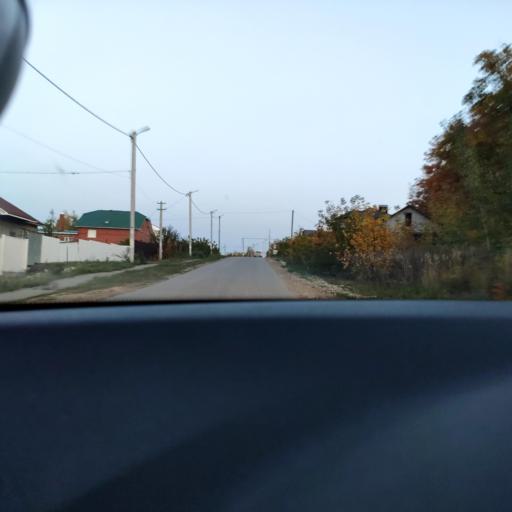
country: RU
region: Samara
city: Novosemeykino
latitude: 53.3827
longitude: 50.3209
